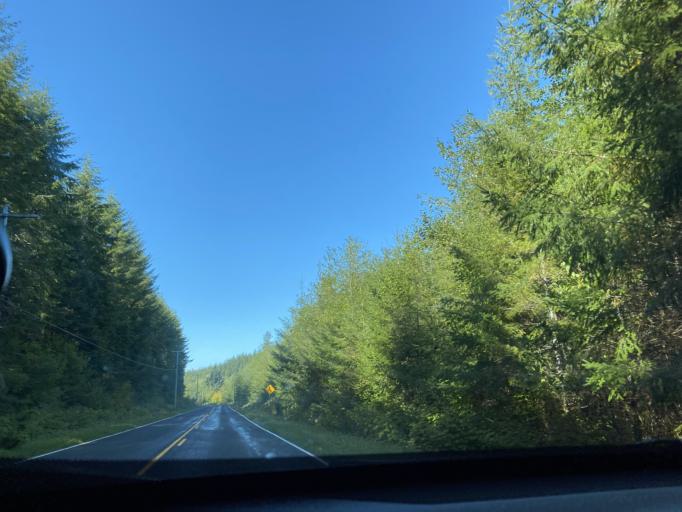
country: US
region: Washington
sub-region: Clallam County
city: Forks
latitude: 47.9507
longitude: -124.4728
